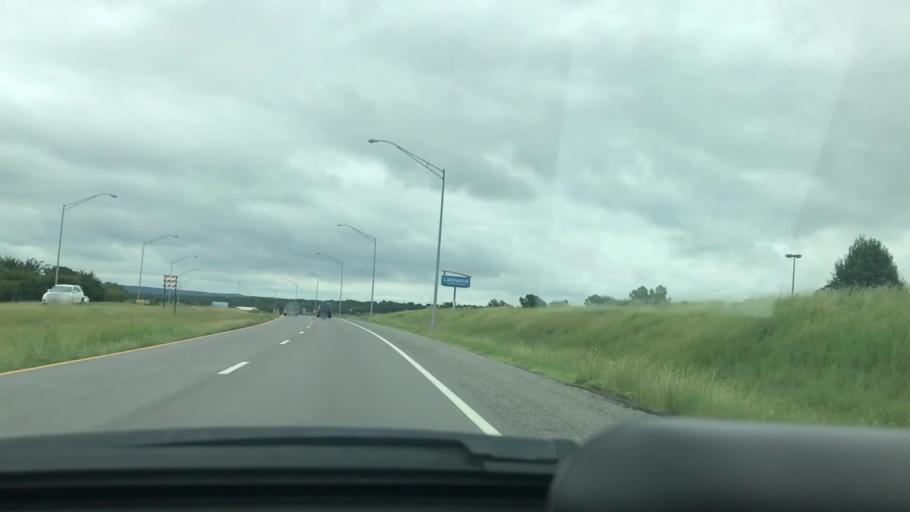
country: US
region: Oklahoma
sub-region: Pittsburg County
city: McAlester
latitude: 34.9011
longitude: -95.7514
